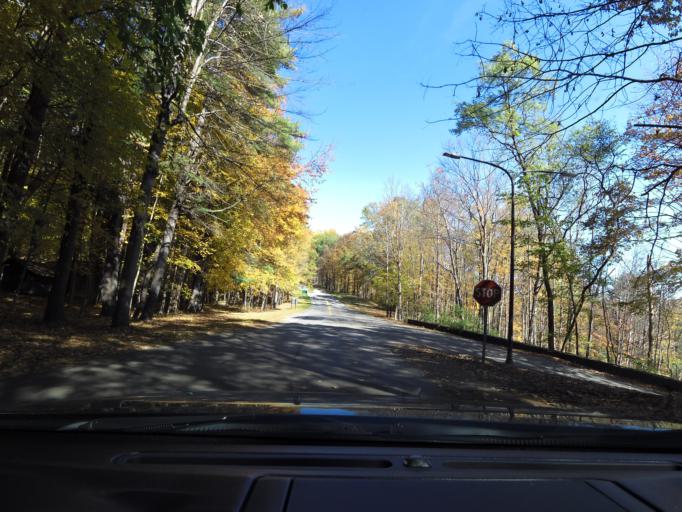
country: US
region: New York
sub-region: Wyoming County
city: Castile
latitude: 42.5905
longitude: -78.0134
